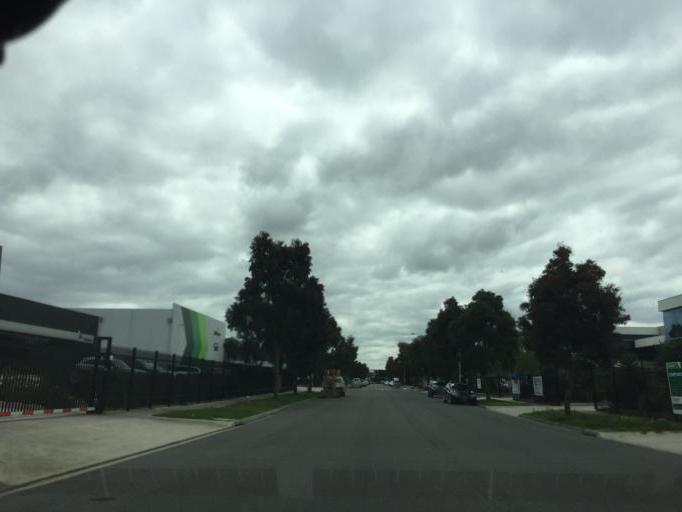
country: AU
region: Victoria
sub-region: Brimbank
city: Brooklyn
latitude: -37.8147
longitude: 144.8210
